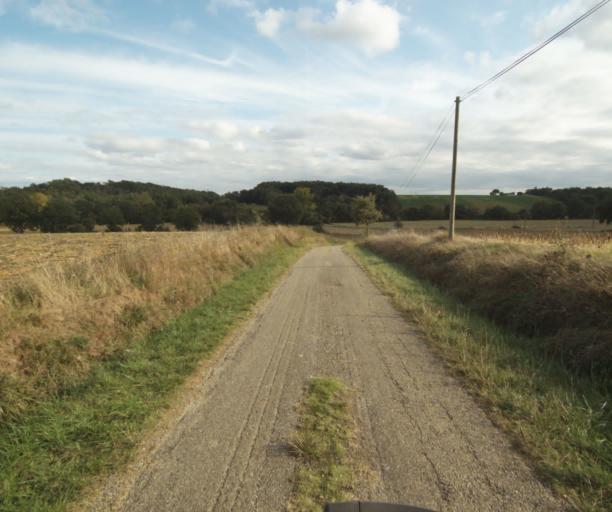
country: FR
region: Midi-Pyrenees
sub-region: Departement du Tarn-et-Garonne
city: Verdun-sur-Garonne
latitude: 43.8390
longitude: 1.1475
